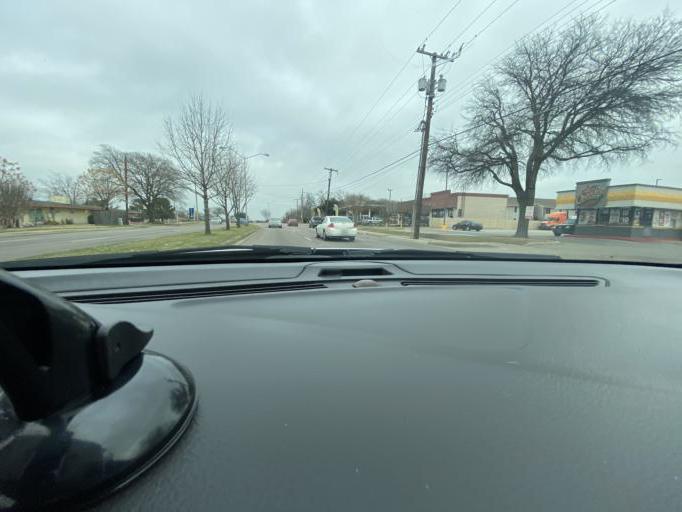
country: US
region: Texas
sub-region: Dallas County
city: Highland Park
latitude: 32.8029
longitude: -96.7126
